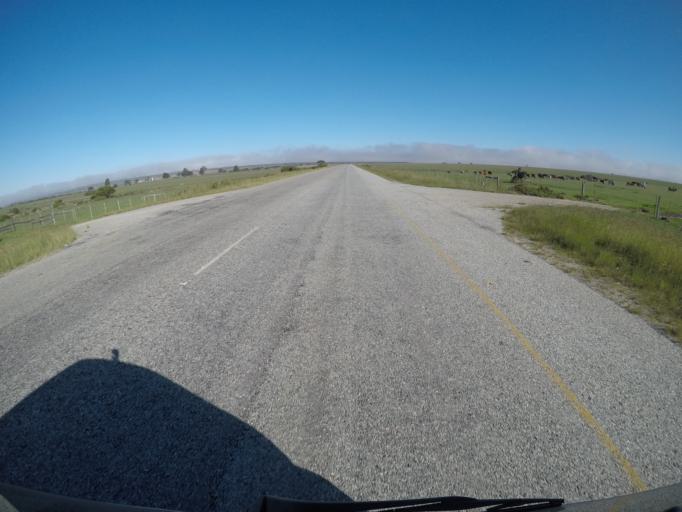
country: ZA
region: Western Cape
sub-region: Eden District Municipality
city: Mossel Bay
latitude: -34.1720
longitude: 22.0142
